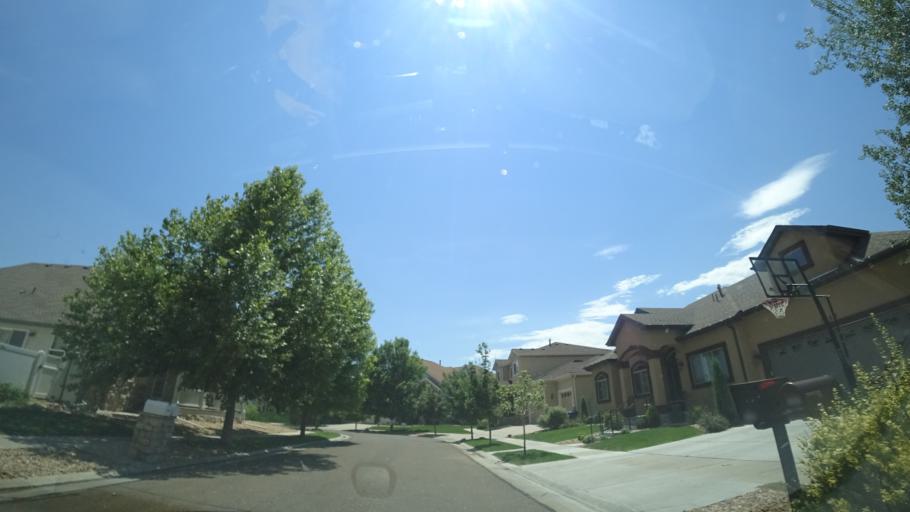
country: US
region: Colorado
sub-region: Jefferson County
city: Lakewood
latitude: 39.6940
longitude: -105.0873
